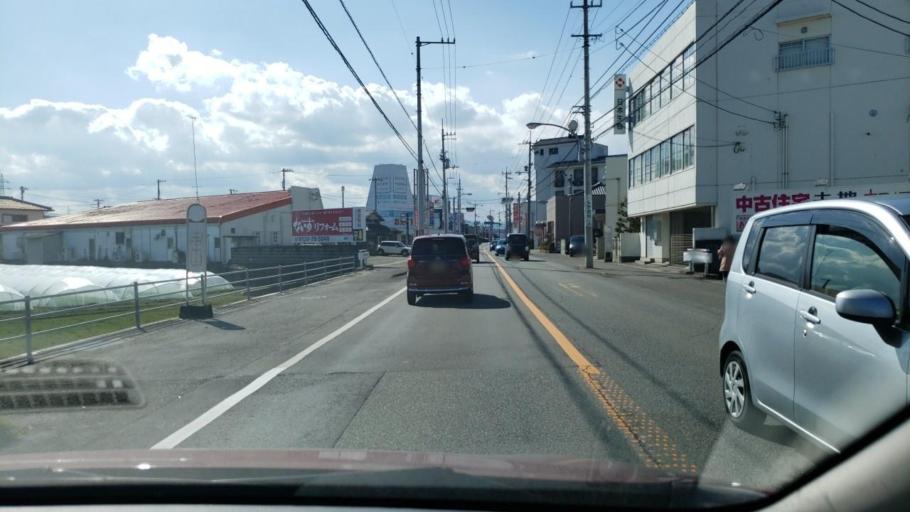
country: JP
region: Tokushima
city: Ishii
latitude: 34.1318
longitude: 134.4875
